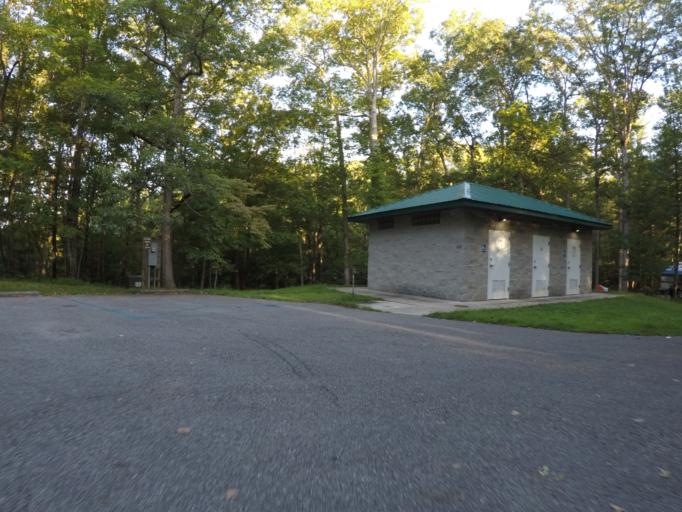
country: US
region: Ohio
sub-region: Lawrence County
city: Ironton
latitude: 38.6118
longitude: -82.6194
